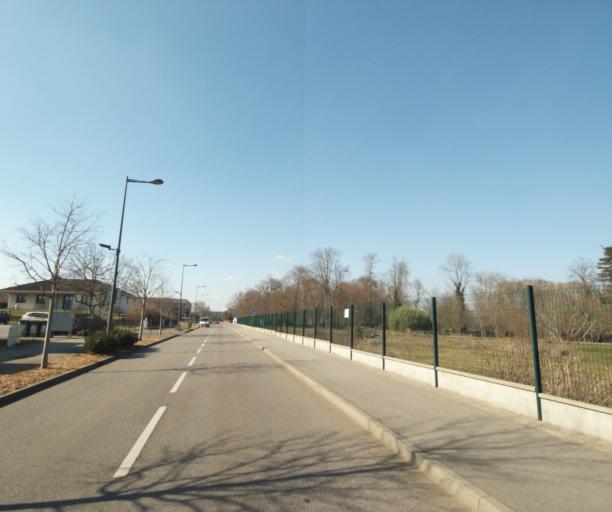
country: FR
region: Lorraine
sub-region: Departement de Meurthe-et-Moselle
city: Heillecourt
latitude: 48.6608
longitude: 6.1962
